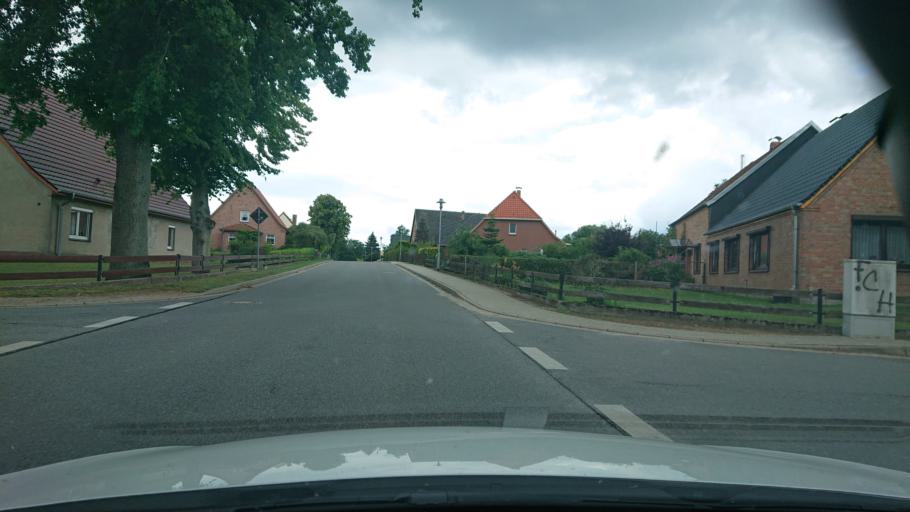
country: DE
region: Mecklenburg-Vorpommern
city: Eldena
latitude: 53.3307
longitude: 11.3900
